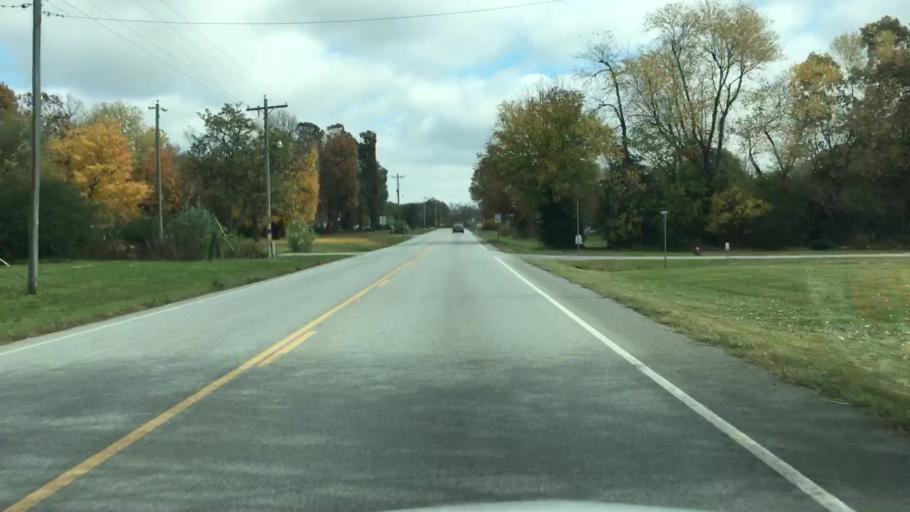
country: US
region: Arkansas
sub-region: Benton County
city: Centerton
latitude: 36.2616
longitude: -94.3568
